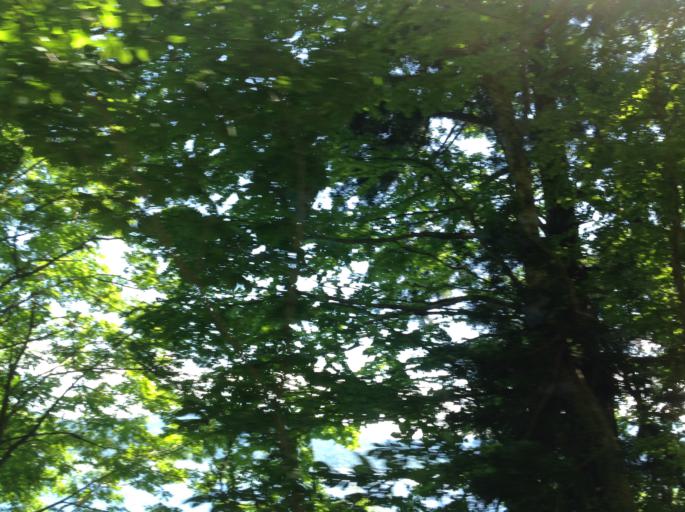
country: JP
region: Akita
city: Kakunodatemachi
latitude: 39.7081
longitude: 140.6387
